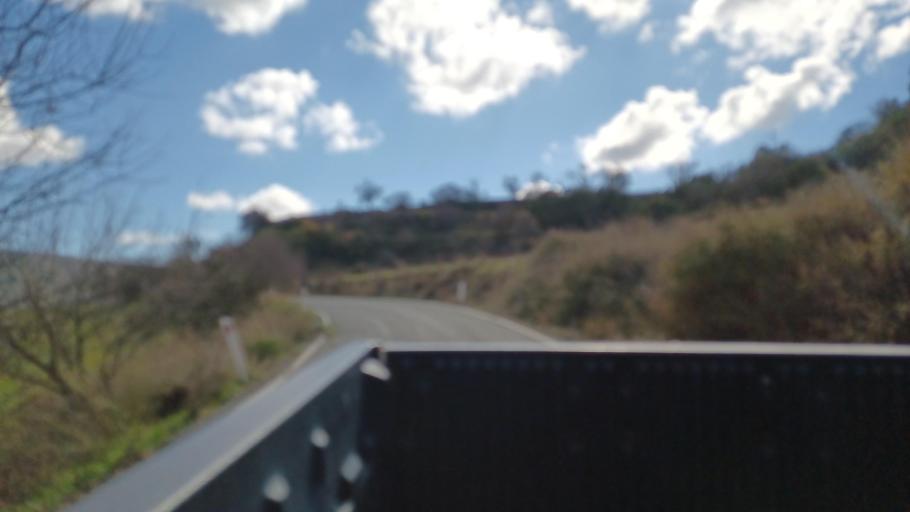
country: CY
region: Limassol
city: Pachna
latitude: 34.7802
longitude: 32.7419
